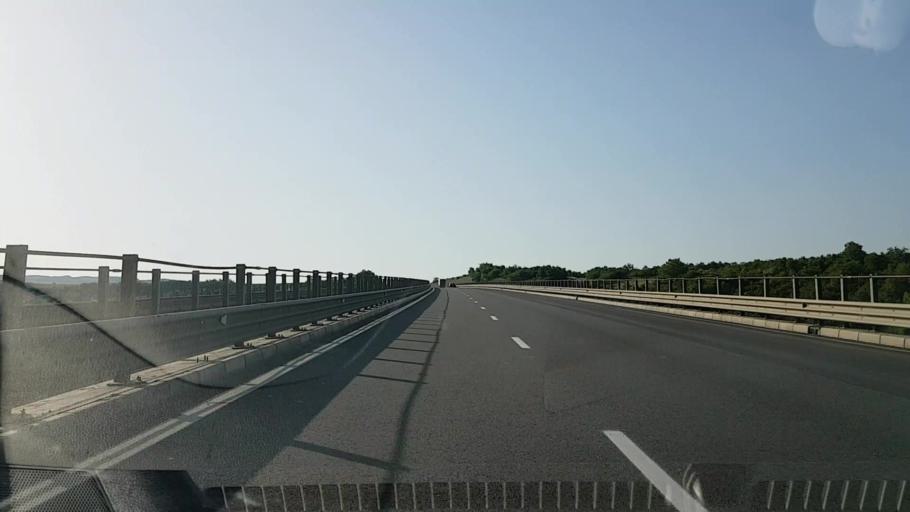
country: RO
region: Cluj
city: Turda
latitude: 46.5616
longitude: 23.7606
